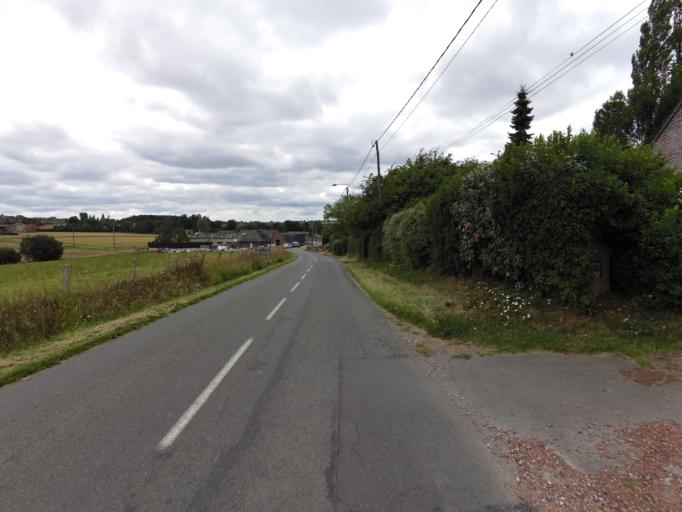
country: FR
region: Nord-Pas-de-Calais
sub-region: Departement du Nord
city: Boeschepe
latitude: 50.8058
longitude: 2.6746
